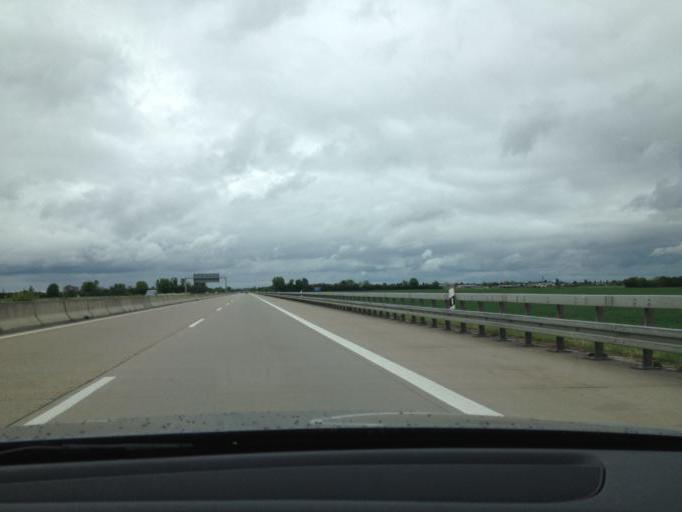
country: DE
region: Baden-Wuerttemberg
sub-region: Karlsruhe Region
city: Eppelheim
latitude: 49.4266
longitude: 8.6192
